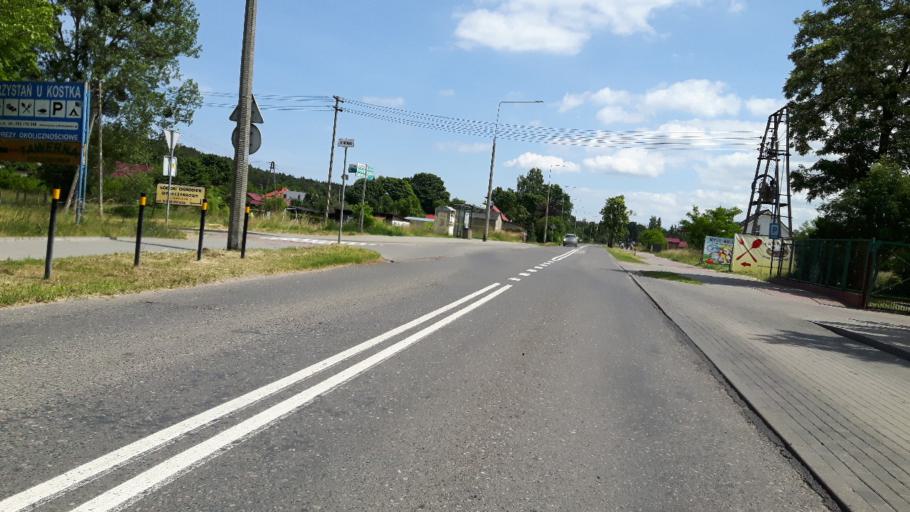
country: PL
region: Pomeranian Voivodeship
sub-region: Powiat gdanski
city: Cedry Wielkie
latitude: 54.3371
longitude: 18.9100
